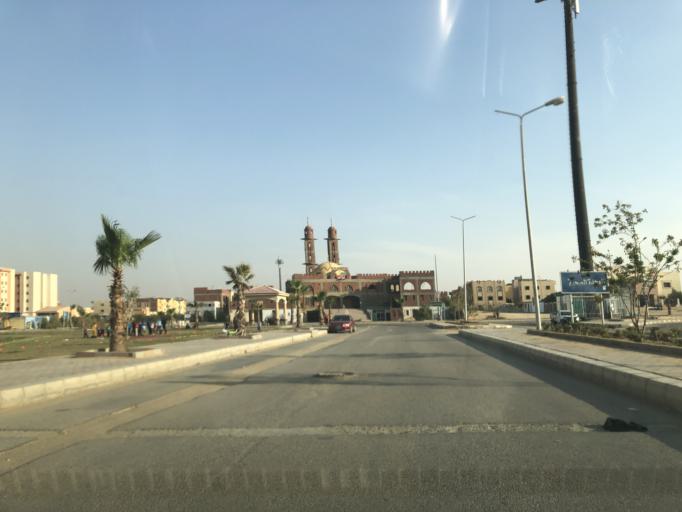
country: EG
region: Al Jizah
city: Madinat Sittah Uktubar
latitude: 29.9055
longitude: 30.9345
